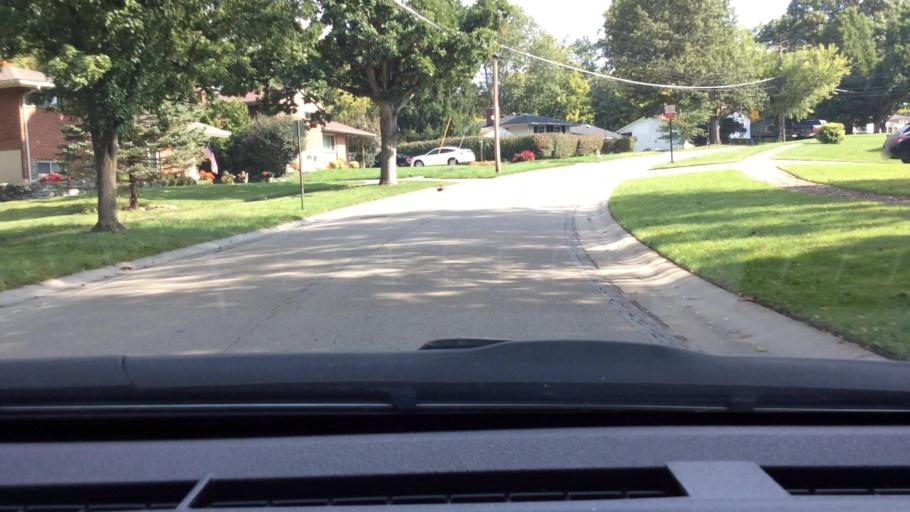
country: US
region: Ohio
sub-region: Hamilton County
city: Greenhills
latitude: 39.2716
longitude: -84.5068
